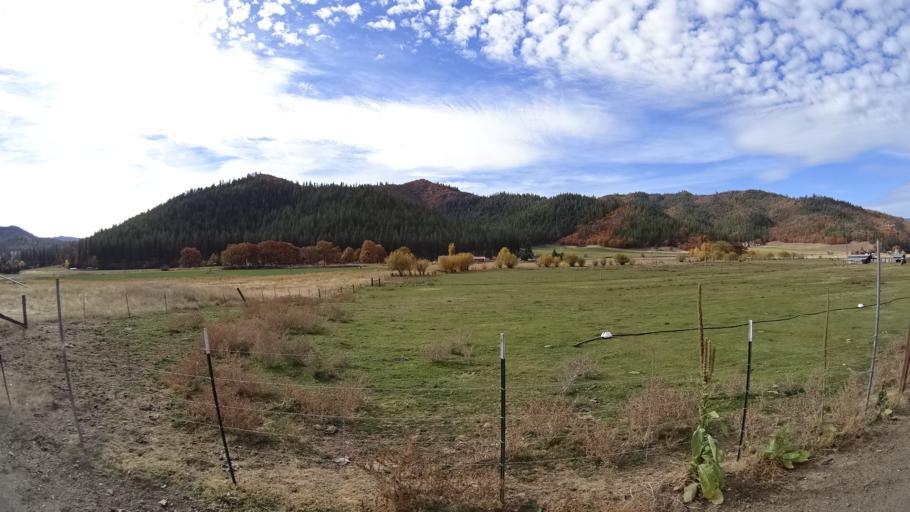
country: US
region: California
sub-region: Siskiyou County
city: Yreka
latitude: 41.6254
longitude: -122.7971
